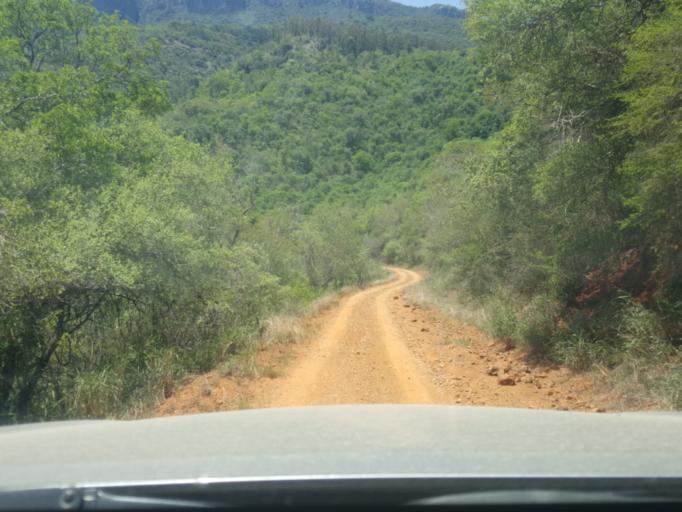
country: ZA
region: Limpopo
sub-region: Mopani District Municipality
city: Hoedspruit
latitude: -24.5923
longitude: 30.8304
